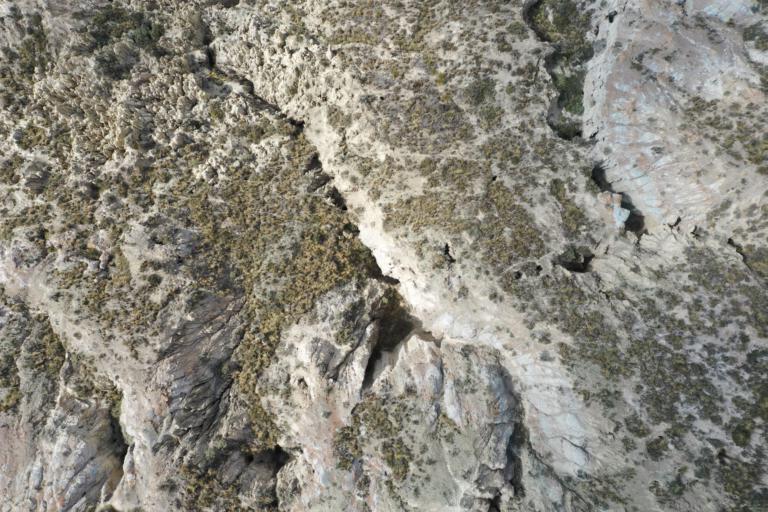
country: BO
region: La Paz
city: La Paz
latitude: -16.5622
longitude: -68.1210
